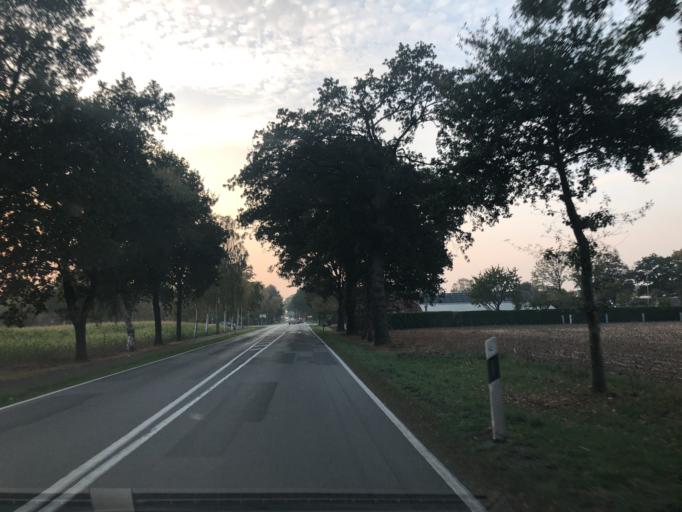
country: DE
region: Lower Saxony
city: Bosel
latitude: 53.0047
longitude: 7.9669
